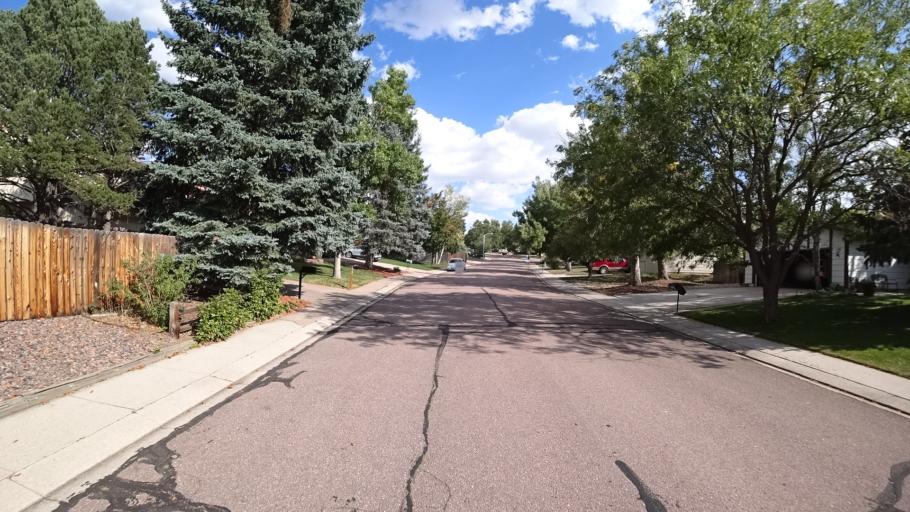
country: US
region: Colorado
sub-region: El Paso County
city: Cimarron Hills
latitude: 38.8735
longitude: -104.7370
